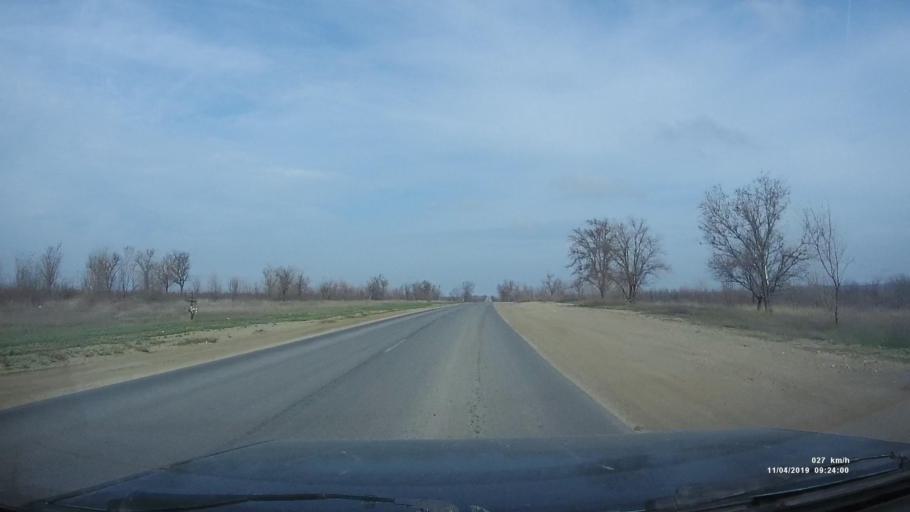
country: RU
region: Rostov
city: Staraya Stanitsa
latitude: 48.2459
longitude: 40.3861
